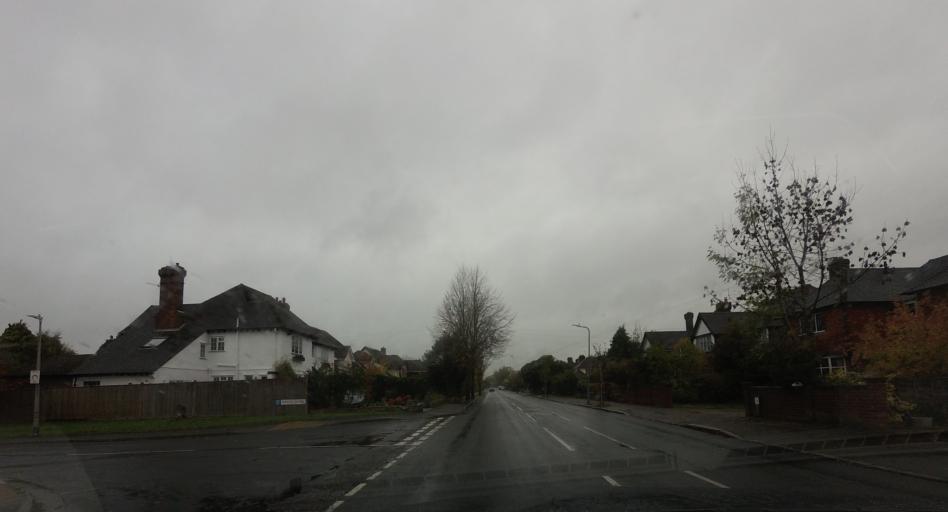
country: GB
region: England
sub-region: Kent
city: Tonbridge
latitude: 51.2056
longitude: 0.2855
